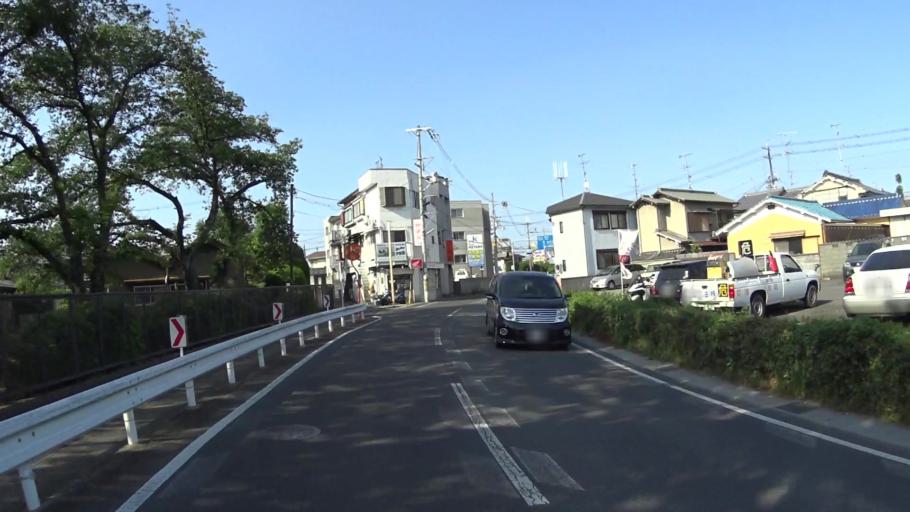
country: JP
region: Kyoto
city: Muko
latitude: 34.9284
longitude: 135.6983
